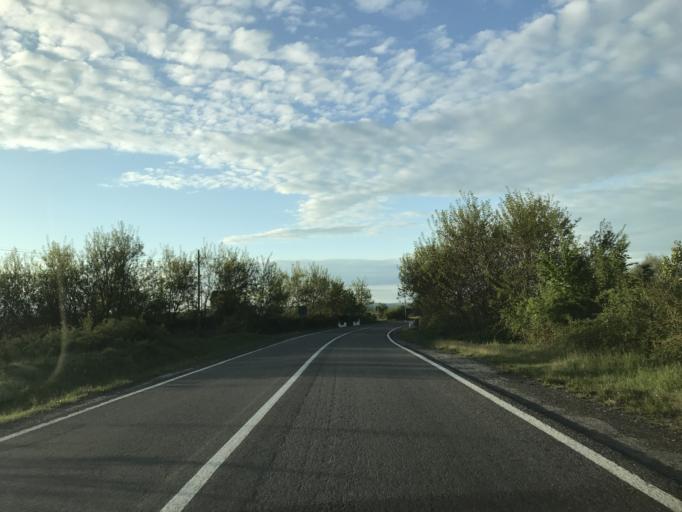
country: RO
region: Sibiu
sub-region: Comuna Cartisoara
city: Cartisoara
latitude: 45.7021
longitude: 24.5711
